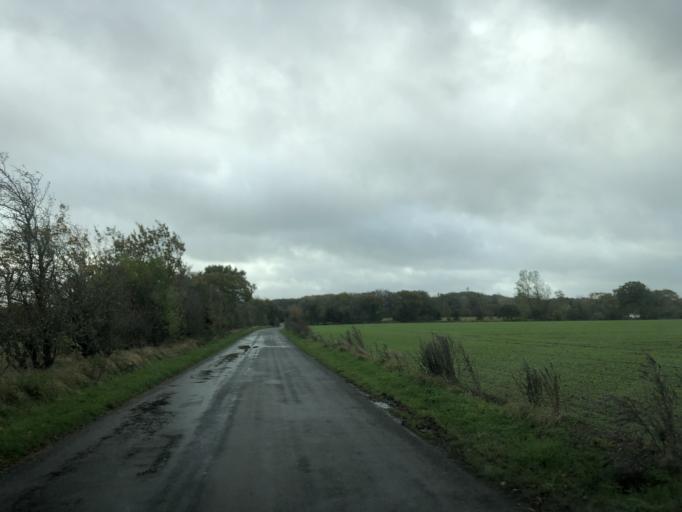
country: DK
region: South Denmark
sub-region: Vejen Kommune
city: Vejen
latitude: 55.4523
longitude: 9.1095
